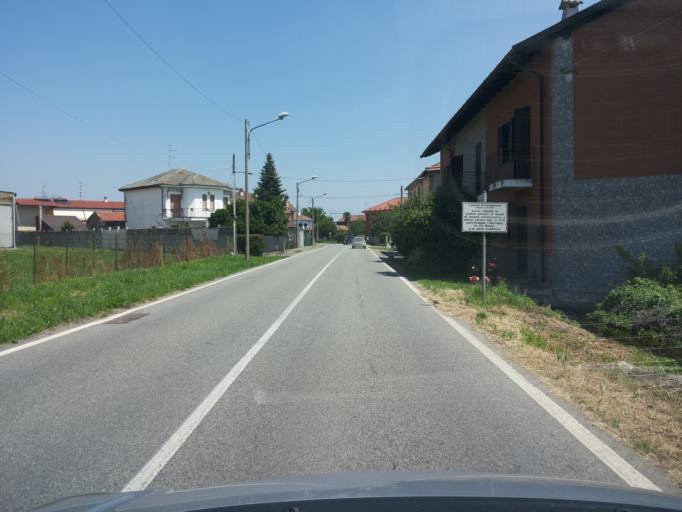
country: IT
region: Piedmont
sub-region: Provincia di Novara
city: Casalvolone
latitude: 45.3957
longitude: 8.4631
